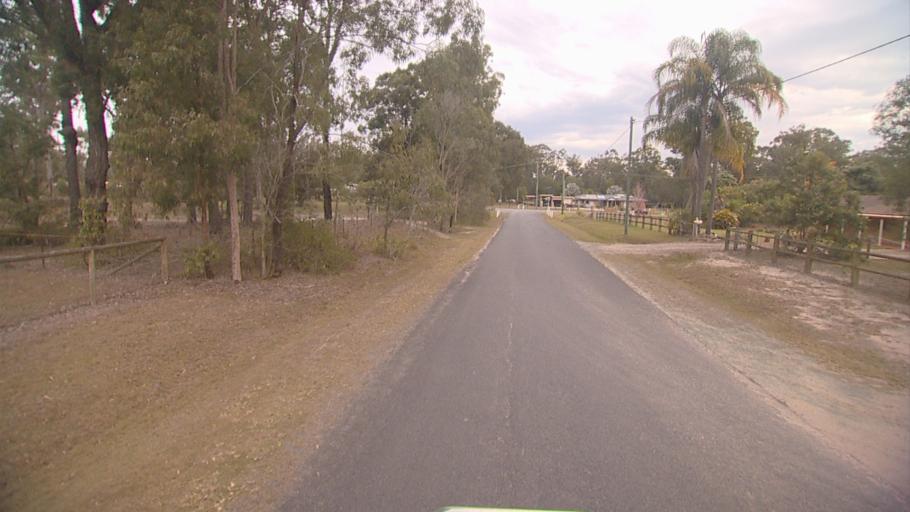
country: AU
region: Queensland
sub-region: Logan
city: Chambers Flat
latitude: -27.8008
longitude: 153.1284
